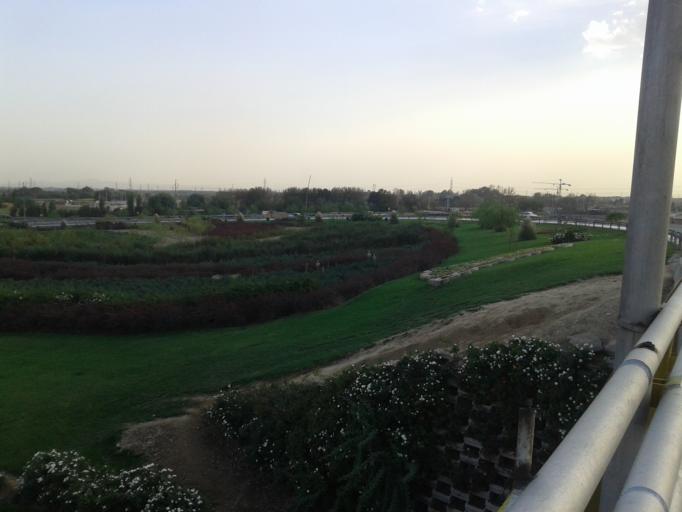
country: IR
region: Tehran
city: Eslamshahr
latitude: 35.6498
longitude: 51.2737
